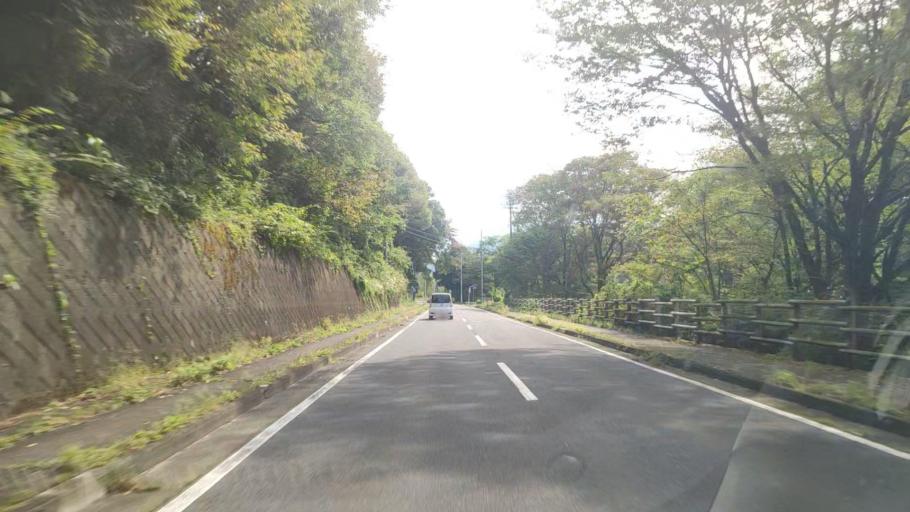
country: JP
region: Gunma
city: Nakanojomachi
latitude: 36.6210
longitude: 138.9325
